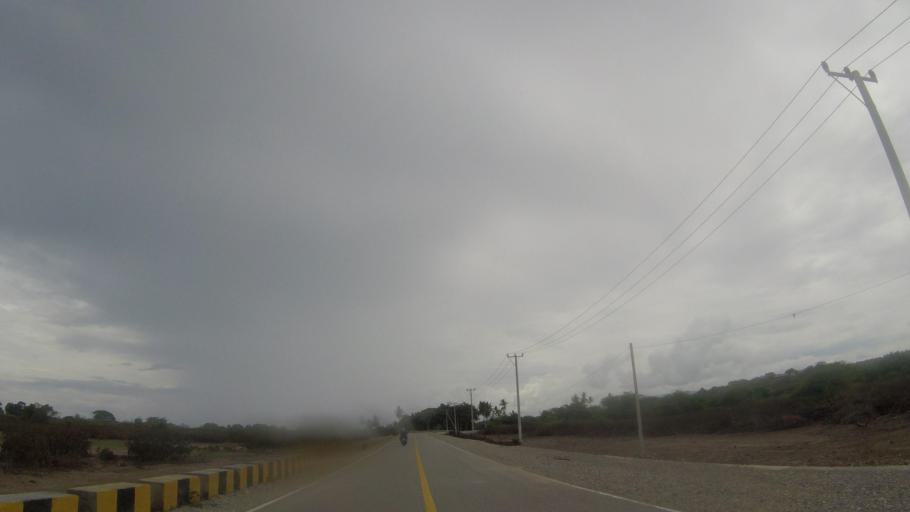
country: TL
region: Baucau
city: Baucau
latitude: -8.4085
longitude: 126.7322
